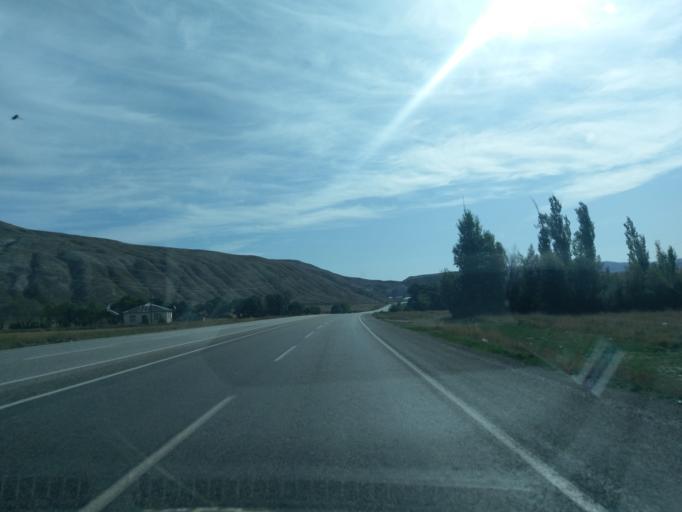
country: TR
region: Sivas
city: Zara
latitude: 39.8618
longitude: 37.8219
